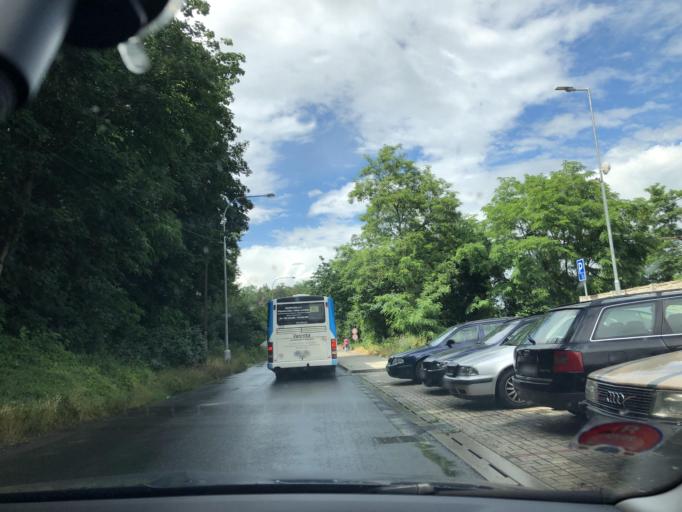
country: CZ
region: Central Bohemia
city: Kralupy nad Vltavou
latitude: 50.2430
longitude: 14.3058
